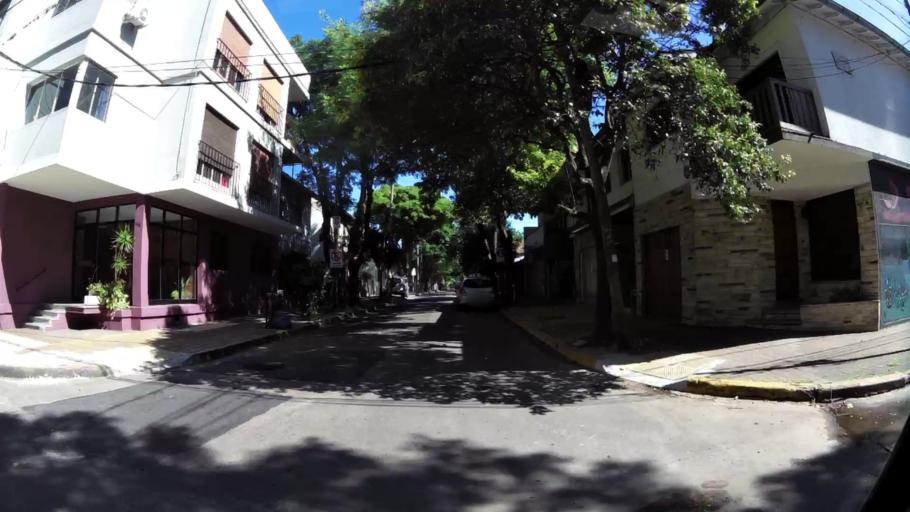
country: AR
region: Buenos Aires
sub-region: Partido de Vicente Lopez
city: Olivos
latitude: -34.5224
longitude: -58.4806
